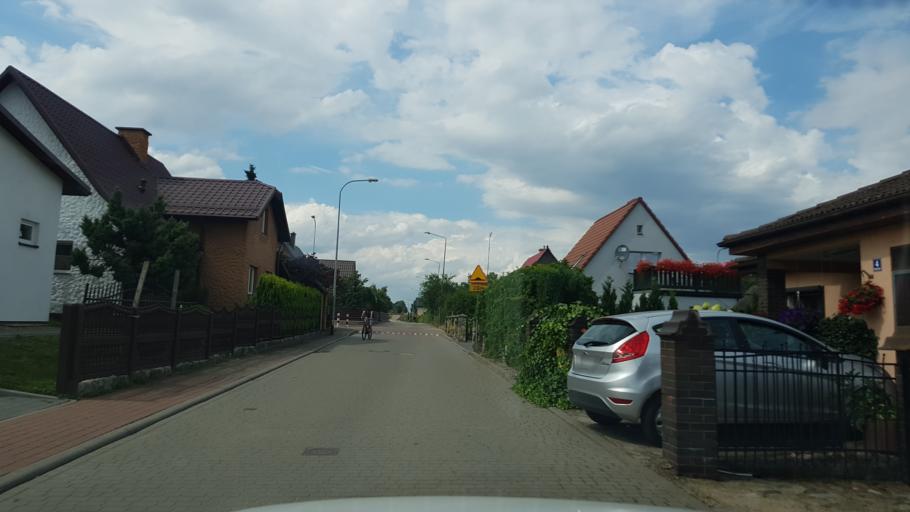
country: PL
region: West Pomeranian Voivodeship
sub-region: Powiat drawski
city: Drawsko Pomorskie
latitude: 53.5432
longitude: 15.8103
